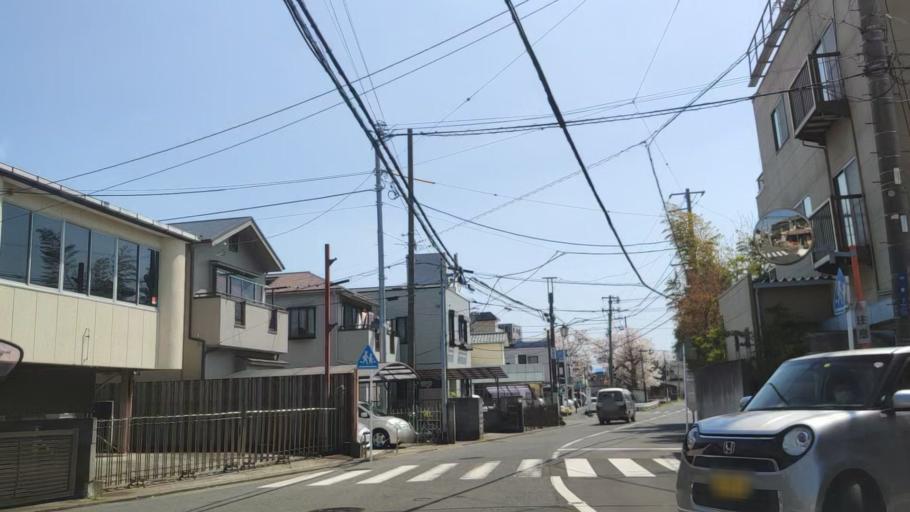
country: JP
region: Kanagawa
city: Hiratsuka
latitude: 35.3352
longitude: 139.3347
